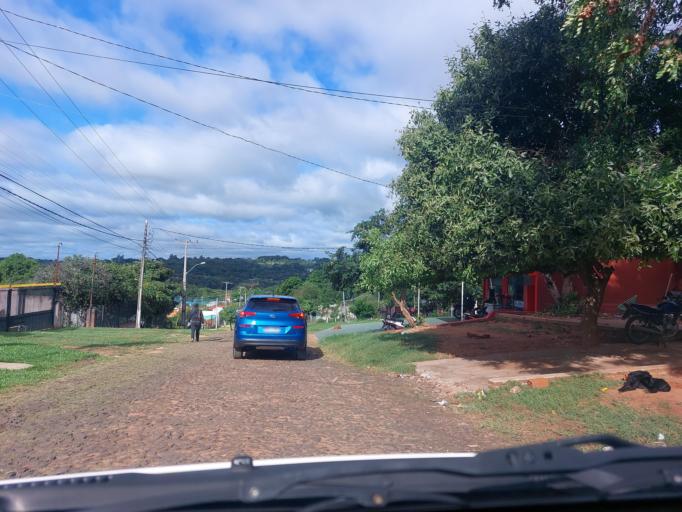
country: PY
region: San Pedro
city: Guayaybi
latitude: -24.6710
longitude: -56.4401
